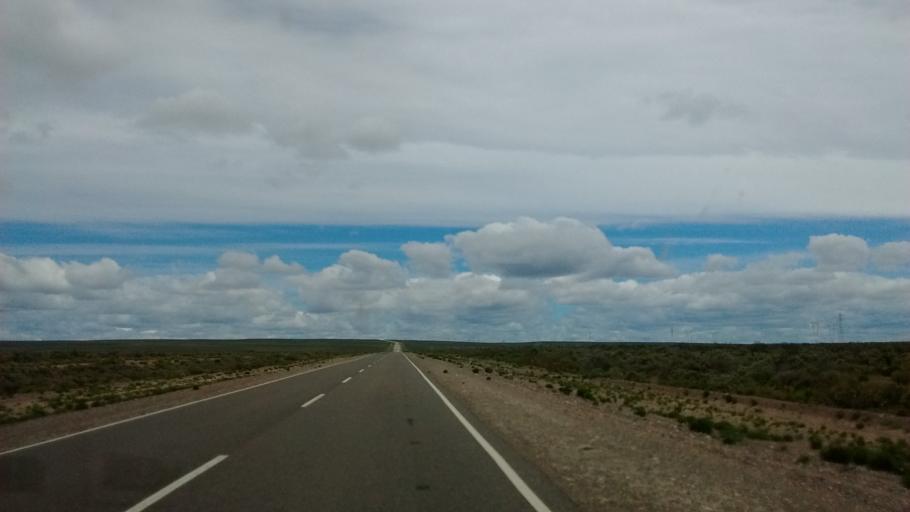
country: AR
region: Neuquen
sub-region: Departamento de Picun Leufu
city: Picun Leufu
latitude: -39.7176
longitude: -69.5333
